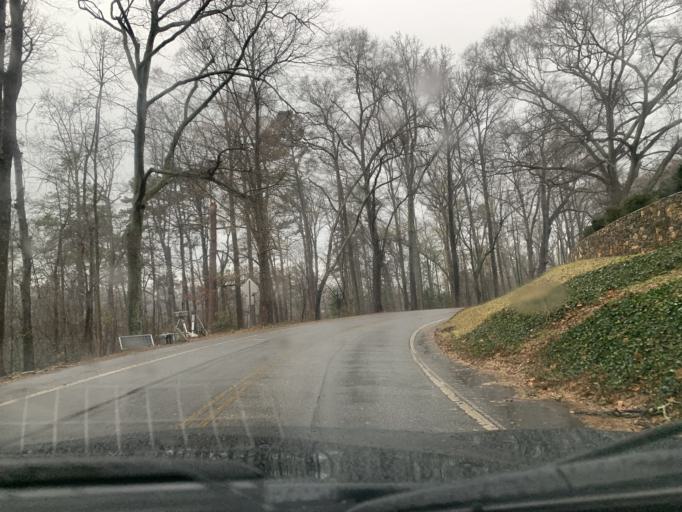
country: US
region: South Carolina
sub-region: Greenville County
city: Greenville
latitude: 34.8447
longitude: -82.3859
